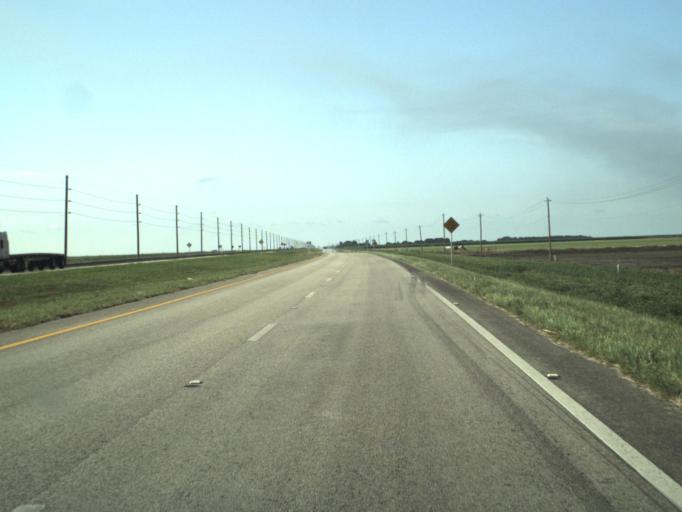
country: US
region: Florida
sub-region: Palm Beach County
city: South Bay
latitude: 26.6417
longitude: -80.7125
